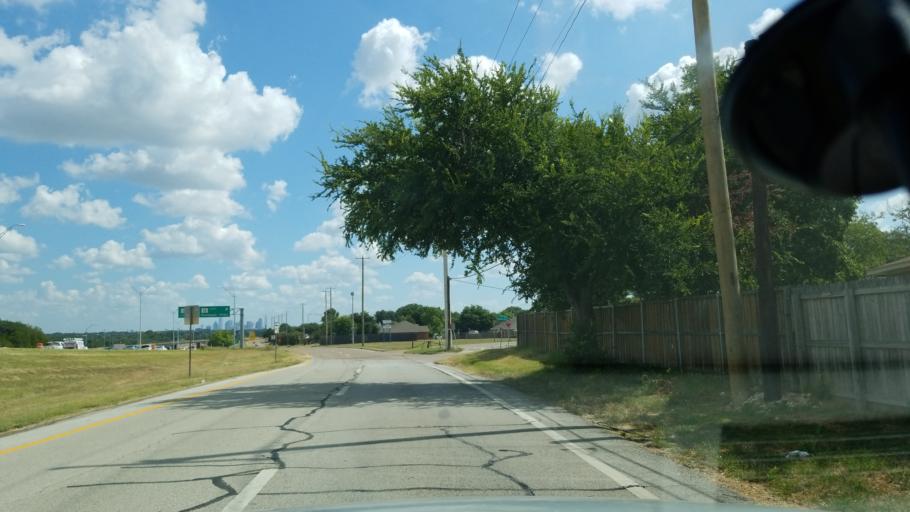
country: US
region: Texas
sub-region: Dallas County
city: Cockrell Hill
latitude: 32.6852
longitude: -96.8488
